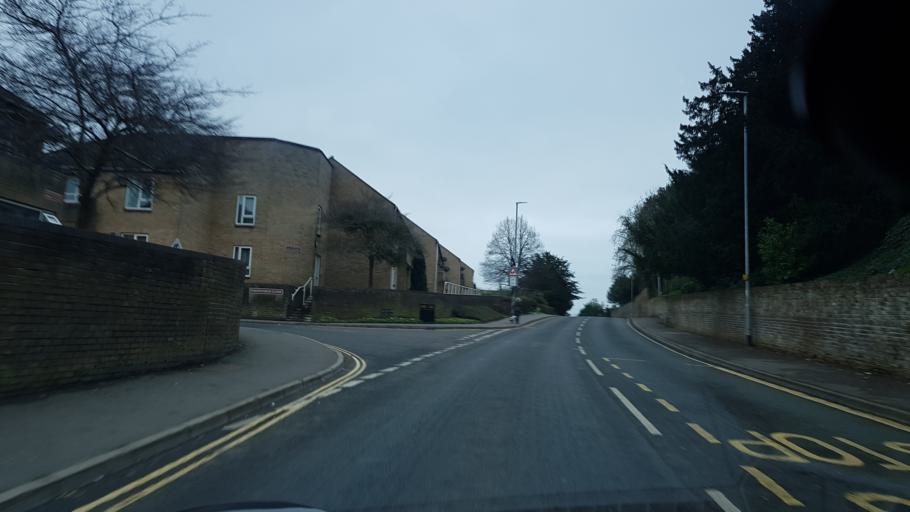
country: GB
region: England
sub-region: Somerset
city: Taunton
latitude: 51.0121
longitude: -3.0954
